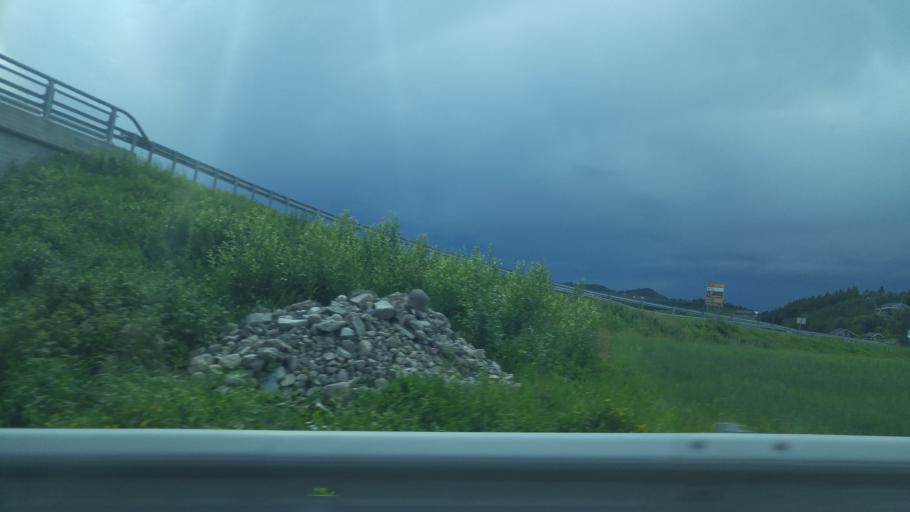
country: NO
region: Nord-Trondelag
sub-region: Stjordal
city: Stjordal
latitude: 63.5282
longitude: 10.8377
